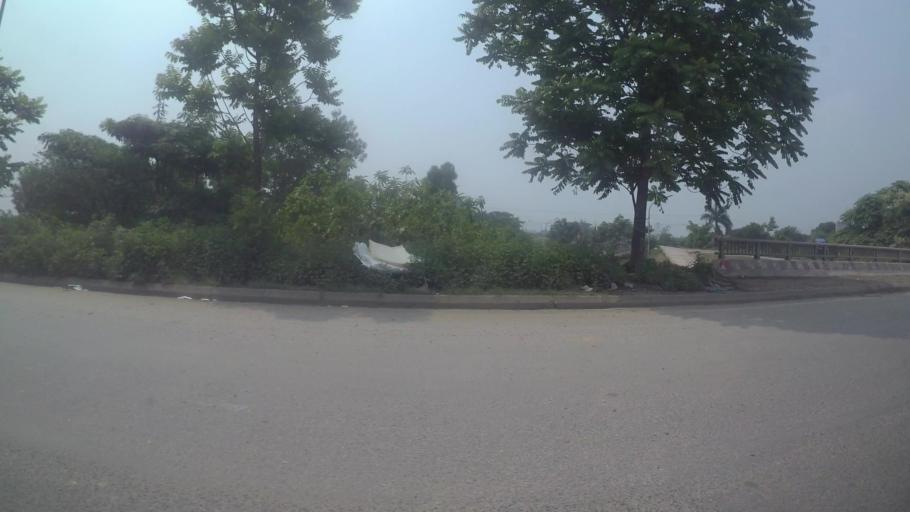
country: VN
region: Ha Noi
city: Quoc Oai
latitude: 21.0071
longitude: 105.7006
